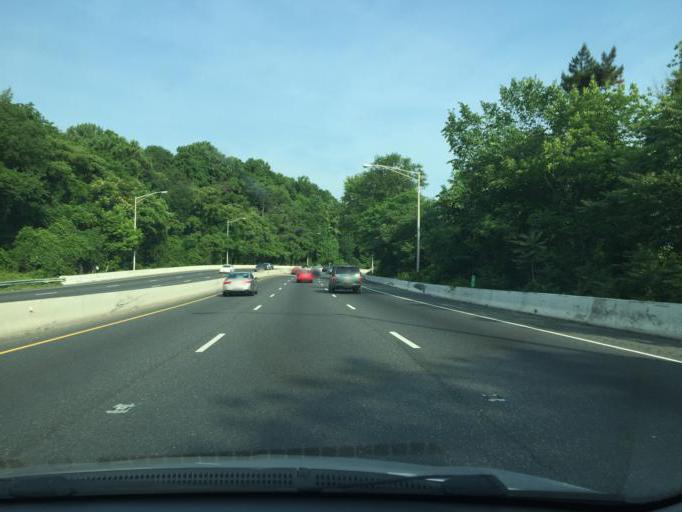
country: US
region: Maryland
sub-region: City of Baltimore
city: Baltimore
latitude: 39.3262
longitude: -76.6374
